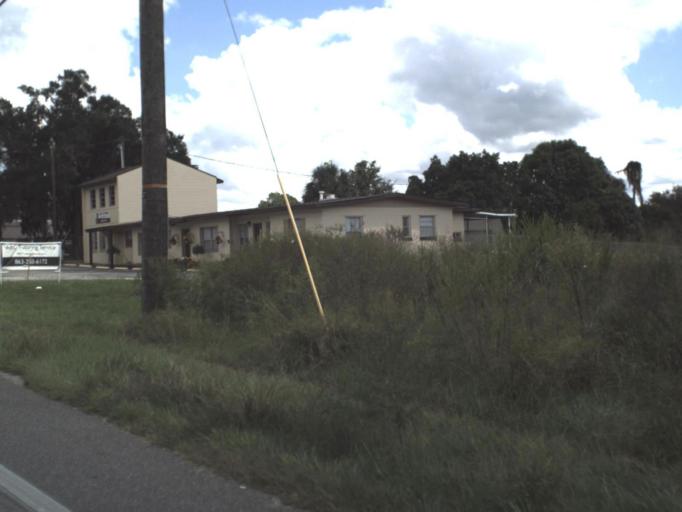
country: US
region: Florida
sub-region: Polk County
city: Cypress Gardens
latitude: 28.0225
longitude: -81.6991
